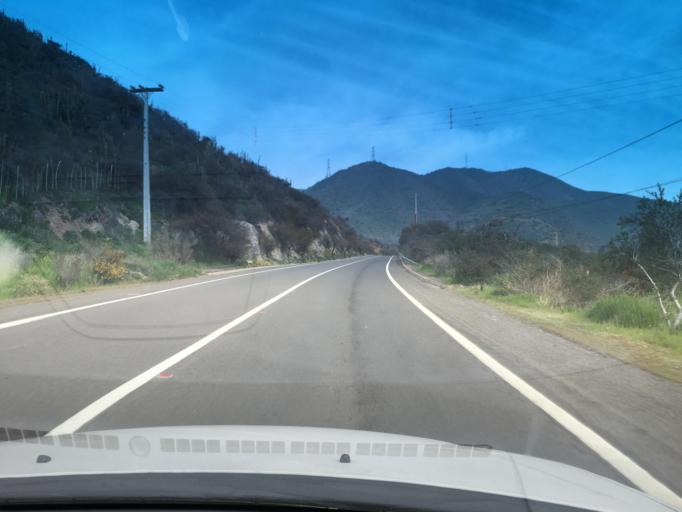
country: CL
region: Santiago Metropolitan
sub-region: Provincia de Chacabuco
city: Lampa
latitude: -33.0768
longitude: -70.9427
